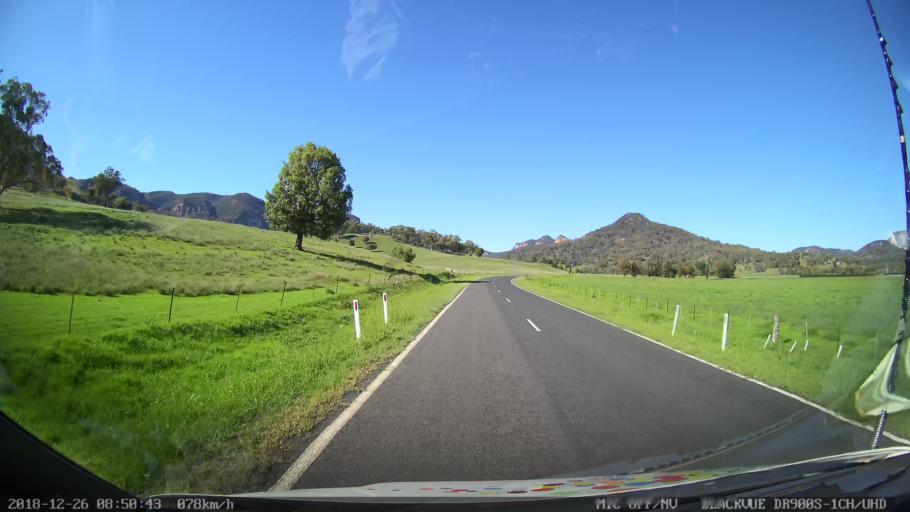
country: AU
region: New South Wales
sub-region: Mid-Western Regional
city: Kandos
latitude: -32.5786
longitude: 150.0934
